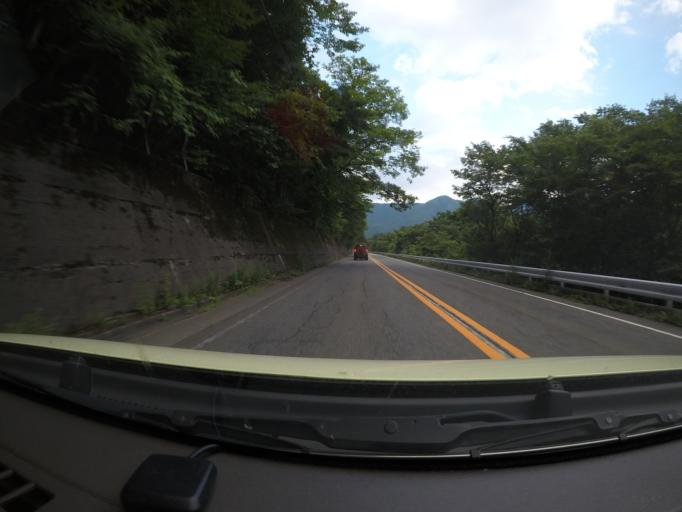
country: JP
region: Tochigi
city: Nikko
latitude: 36.7386
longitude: 139.5377
